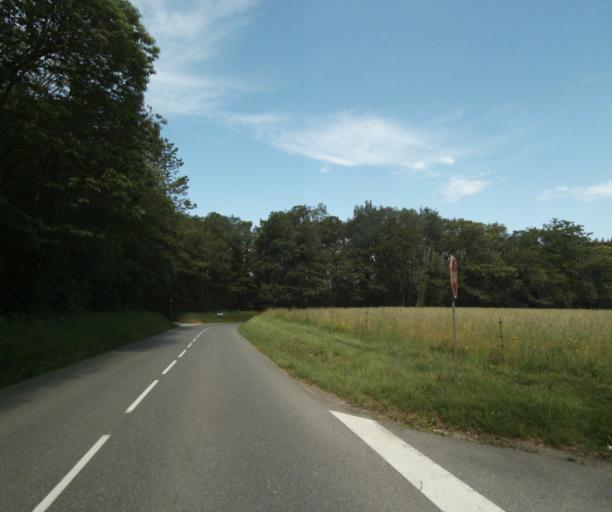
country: FR
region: Rhone-Alpes
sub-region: Departement de la Haute-Savoie
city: Armoy
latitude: 46.3608
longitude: 6.5090
